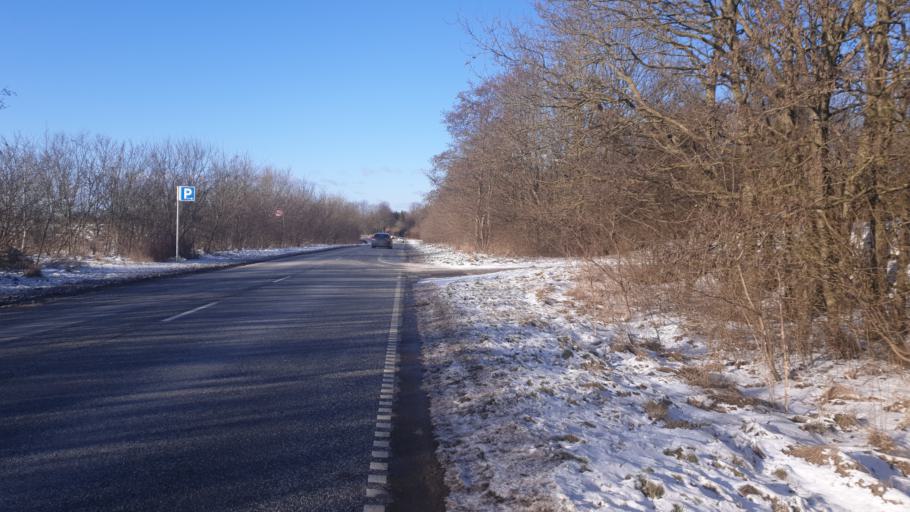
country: DK
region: Central Jutland
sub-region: Hedensted Kommune
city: Hedensted
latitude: 55.7878
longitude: 9.7083
